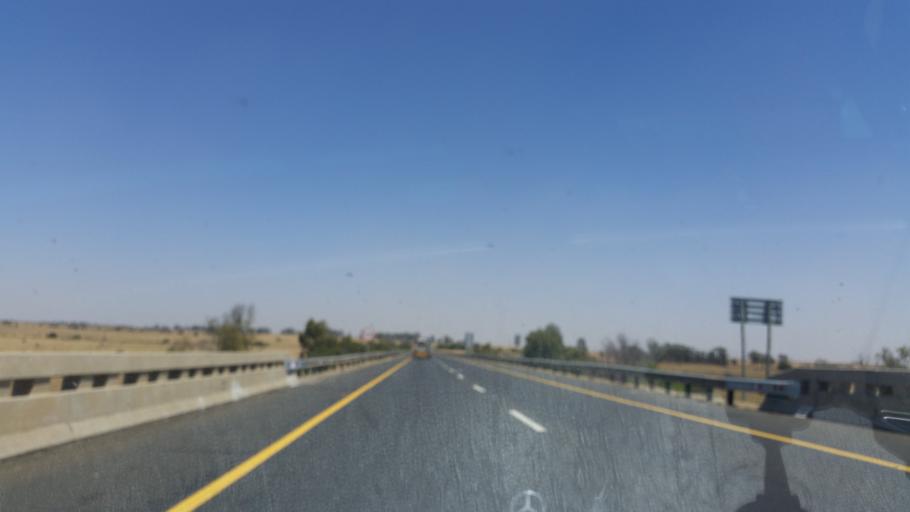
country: ZA
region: Orange Free State
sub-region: Lejweleputswa District Municipality
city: Winburg
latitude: -28.6321
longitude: 26.9030
